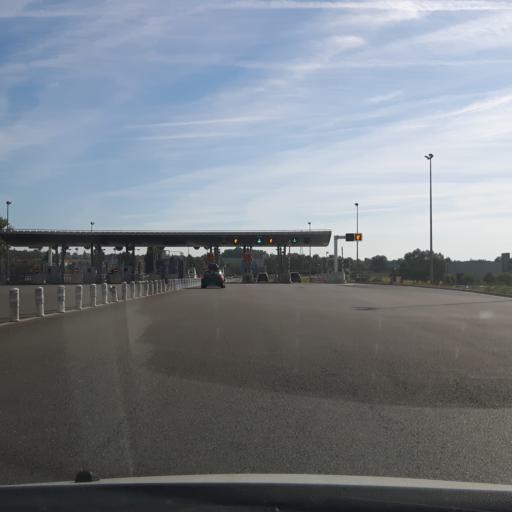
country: FR
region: Midi-Pyrenees
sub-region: Departement de la Haute-Garonne
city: Saint-Jory
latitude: 43.7643
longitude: 1.3794
